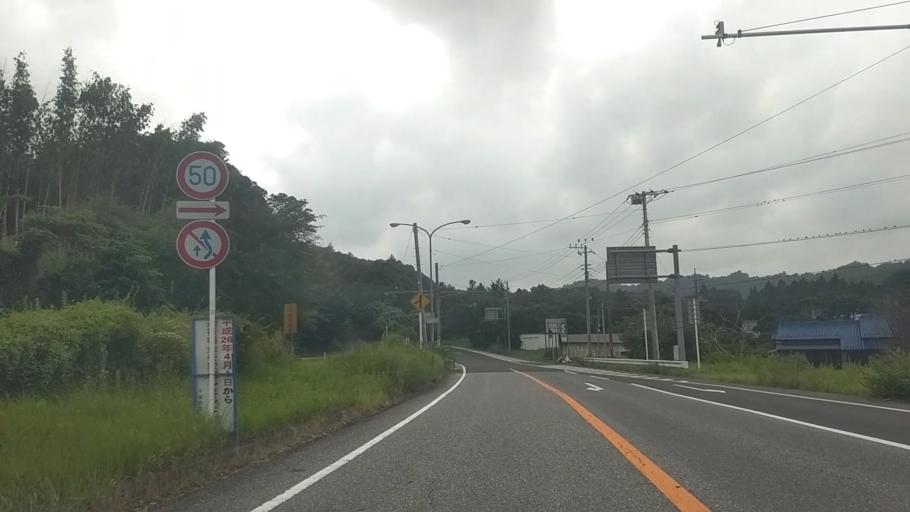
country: JP
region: Chiba
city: Kawaguchi
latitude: 35.2051
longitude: 140.0708
